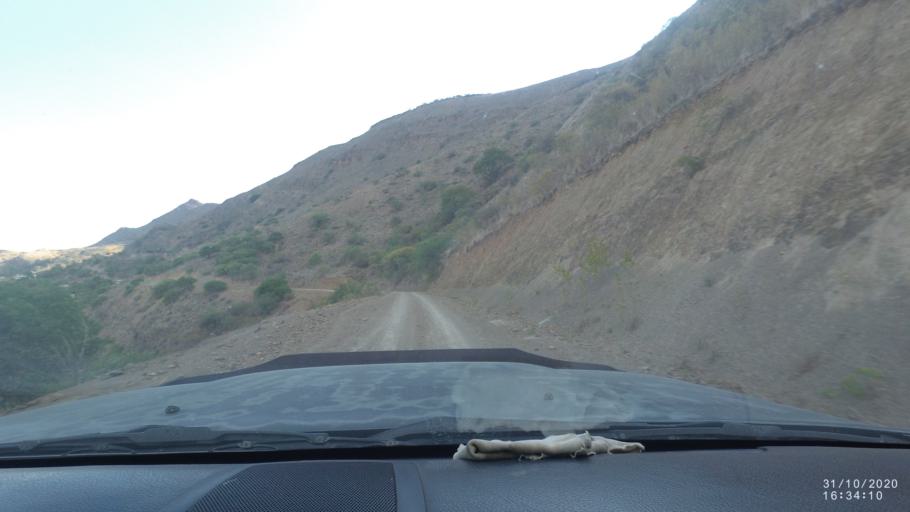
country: BO
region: Chuquisaca
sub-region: Provincia Zudanez
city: Mojocoya
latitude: -18.4468
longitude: -64.5845
